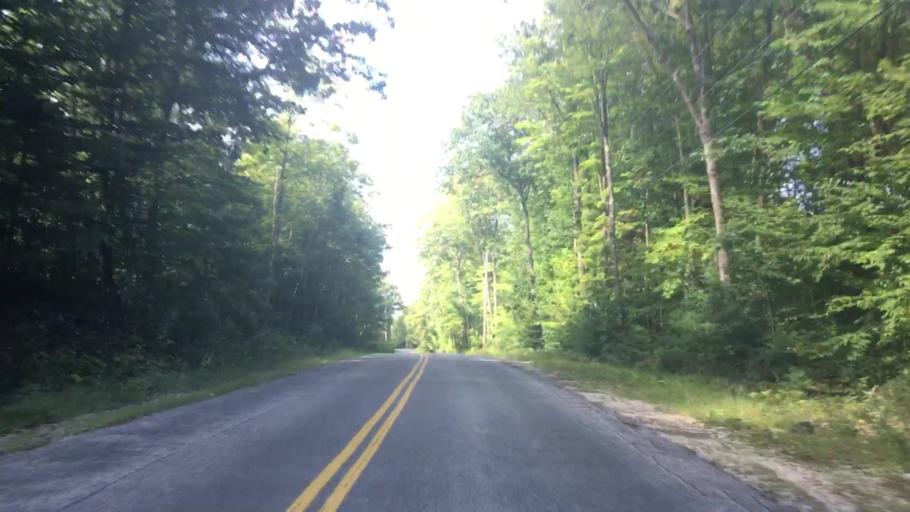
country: US
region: Maine
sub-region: Androscoggin County
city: Poland
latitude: 44.0102
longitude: -70.4156
